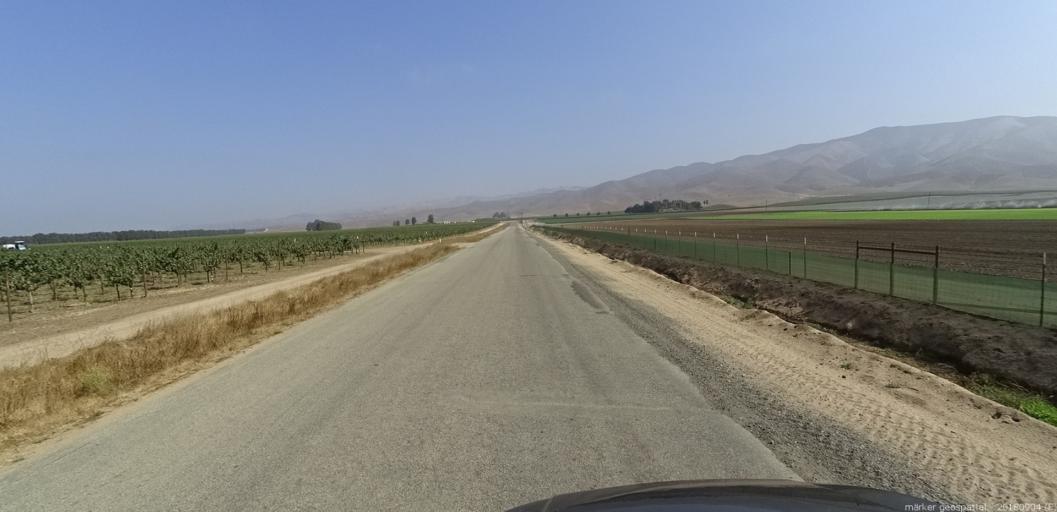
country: US
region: California
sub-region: Monterey County
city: Soledad
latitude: 36.4675
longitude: -121.3518
